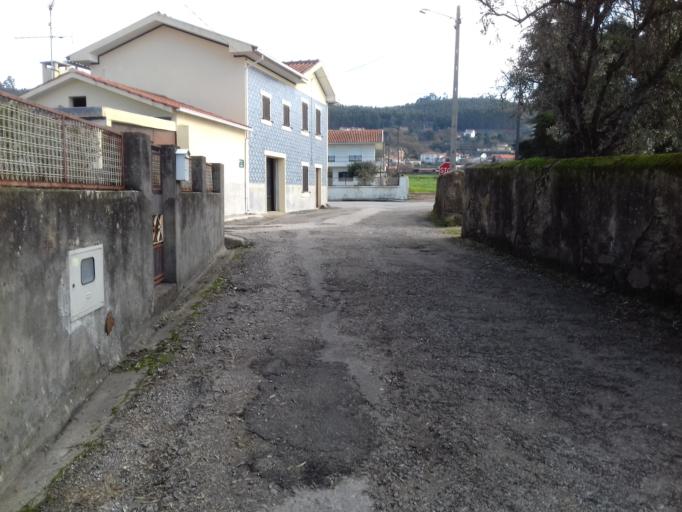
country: PT
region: Aveiro
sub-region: Albergaria-A-Velha
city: Branca
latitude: 40.7644
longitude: -8.4829
